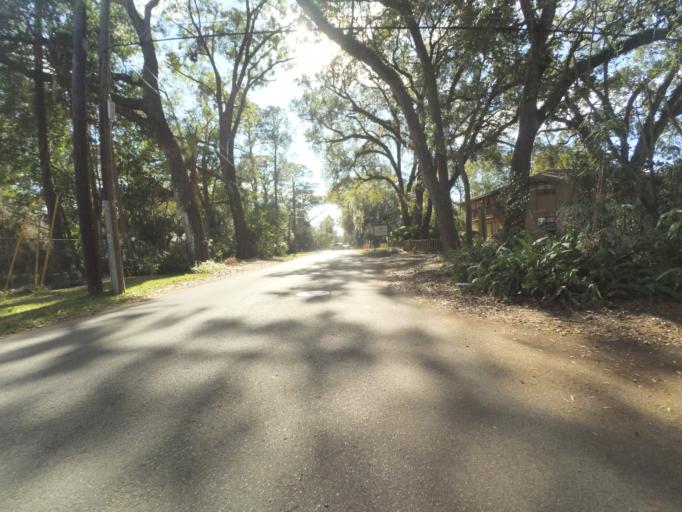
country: US
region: Florida
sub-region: Alachua County
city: Gainesville
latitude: 29.6629
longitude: -82.3372
